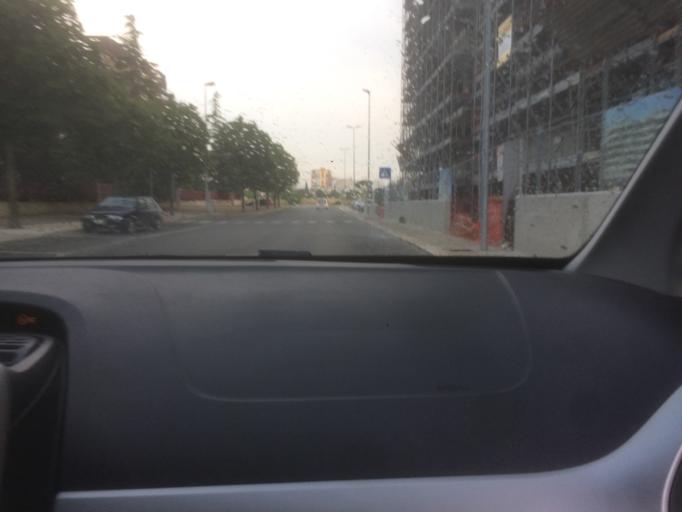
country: IT
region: Apulia
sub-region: Provincia di Bari
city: Triggiano
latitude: 41.0719
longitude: 16.9281
